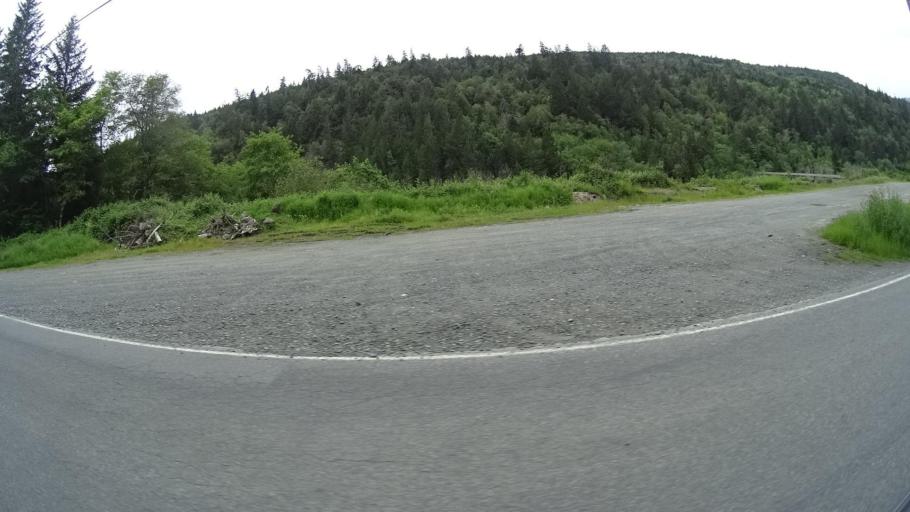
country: US
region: California
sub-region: Humboldt County
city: Willow Creek
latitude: 41.2065
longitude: -123.7541
